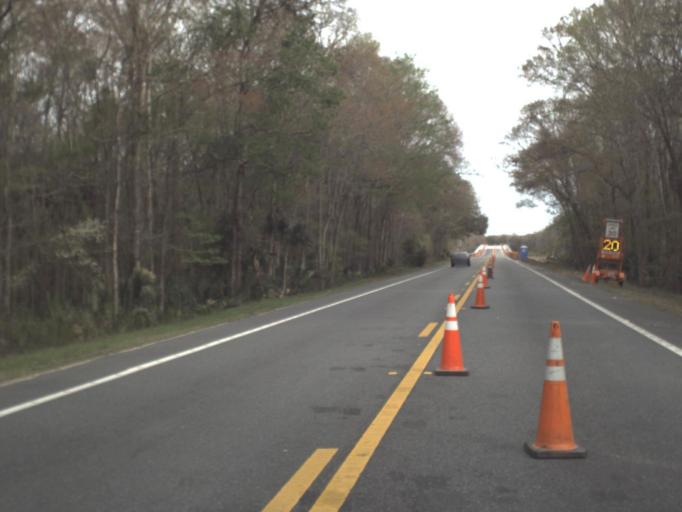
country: US
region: Florida
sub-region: Leon County
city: Woodville
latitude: 30.1489
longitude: -83.9788
